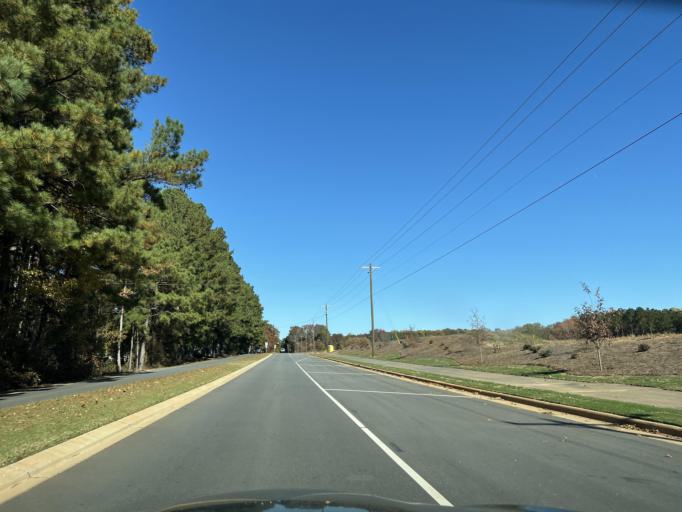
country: US
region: North Carolina
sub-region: Wake County
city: Fuquay-Varina
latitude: 35.6474
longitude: -78.7219
